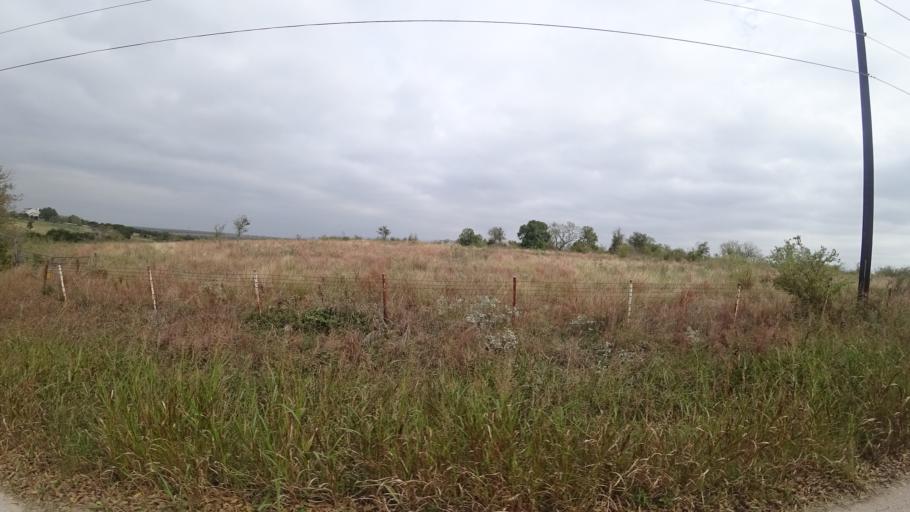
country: US
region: Texas
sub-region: Travis County
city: Pflugerville
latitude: 30.3824
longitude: -97.6082
